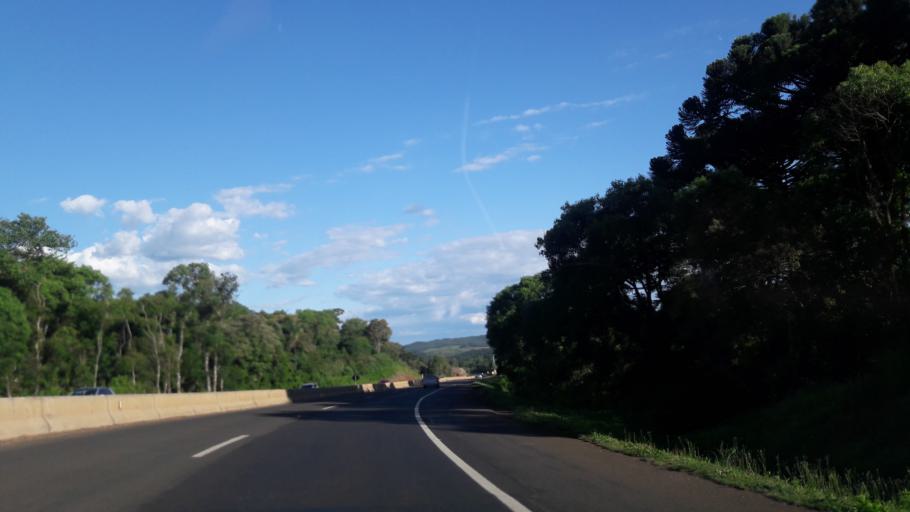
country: BR
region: Parana
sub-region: Guarapuava
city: Guarapuava
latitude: -25.3458
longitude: -51.3835
